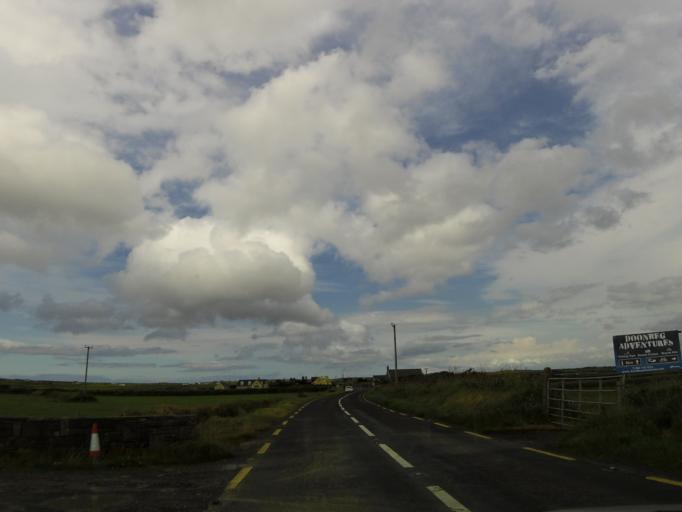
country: IE
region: Munster
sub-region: An Clar
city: Kilrush
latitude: 52.7117
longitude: -9.5912
